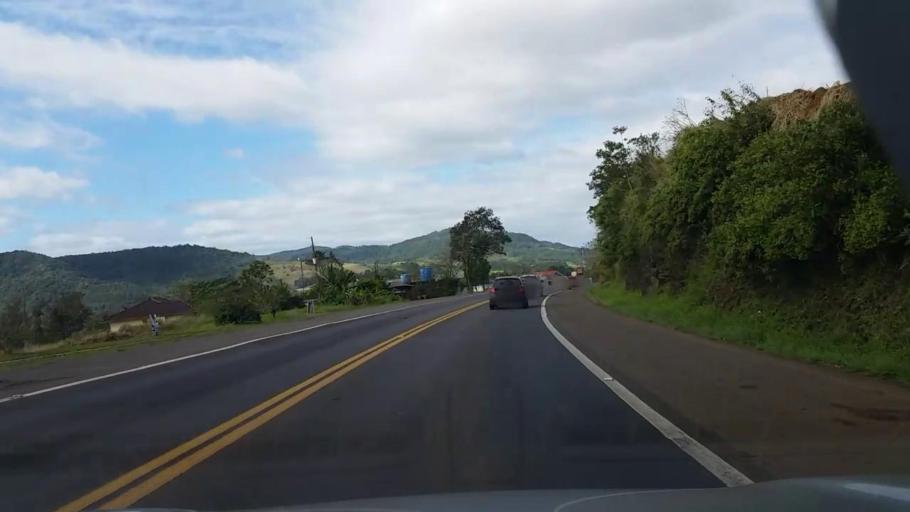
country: BR
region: Rio Grande do Sul
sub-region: Arroio Do Meio
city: Arroio do Meio
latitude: -29.3378
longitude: -52.0806
